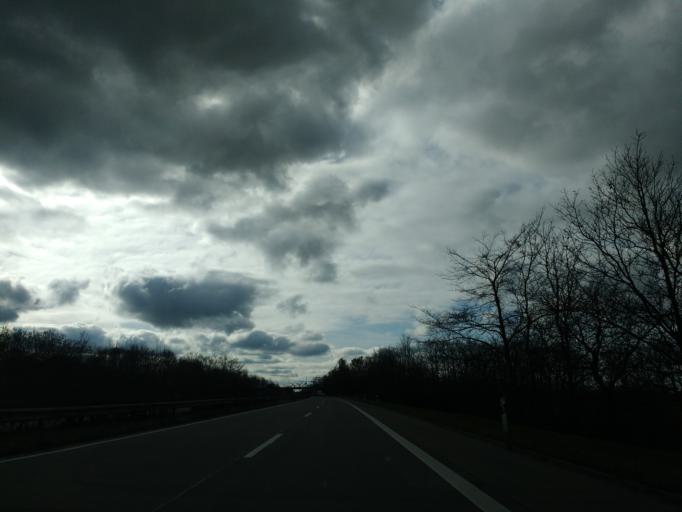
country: DE
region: Lower Saxony
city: Midlum
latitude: 53.7341
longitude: 8.6622
